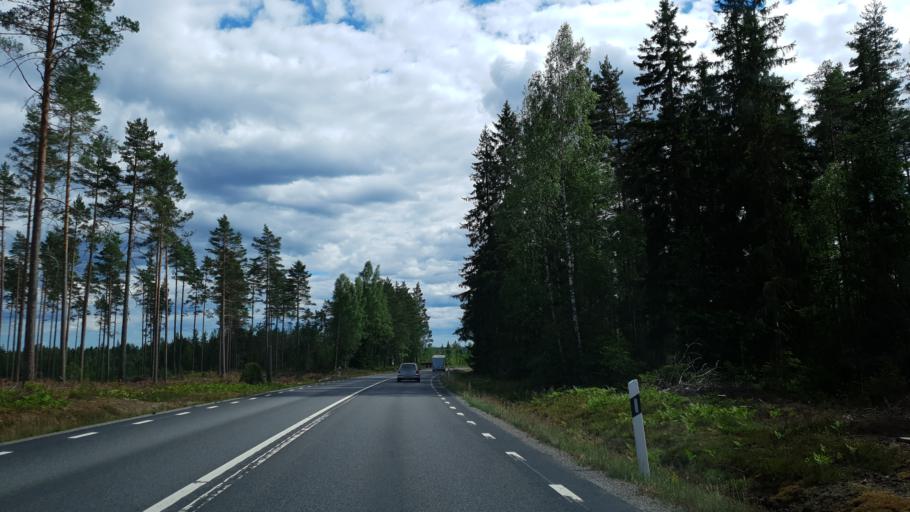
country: SE
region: Kronoberg
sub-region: Lessebo Kommun
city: Lessebo
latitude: 56.8181
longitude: 15.4103
